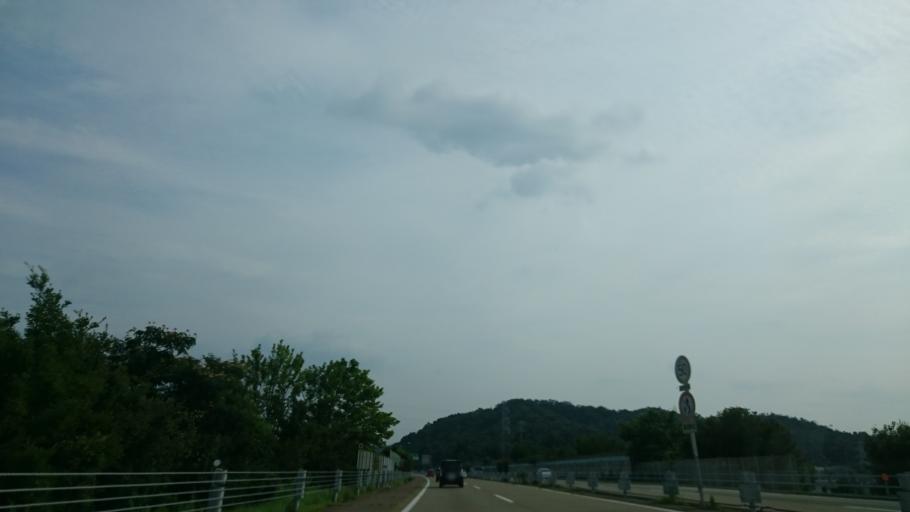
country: JP
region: Gifu
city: Mino
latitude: 35.4956
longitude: 136.8967
